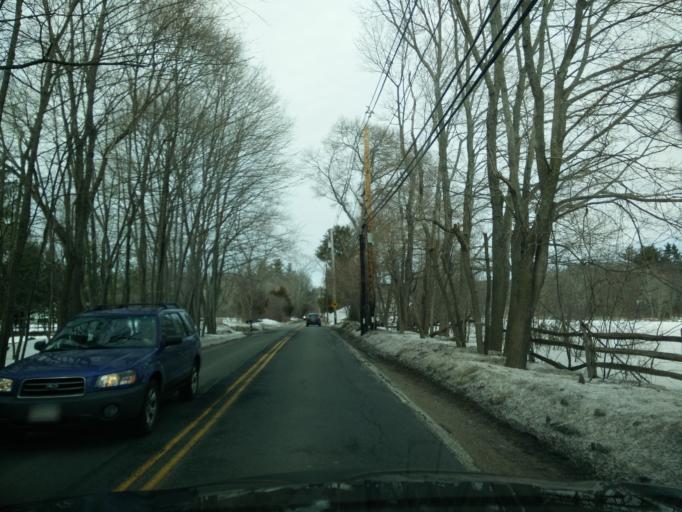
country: US
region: Massachusetts
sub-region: Norfolk County
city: Westwood
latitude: 42.1886
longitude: -71.2479
